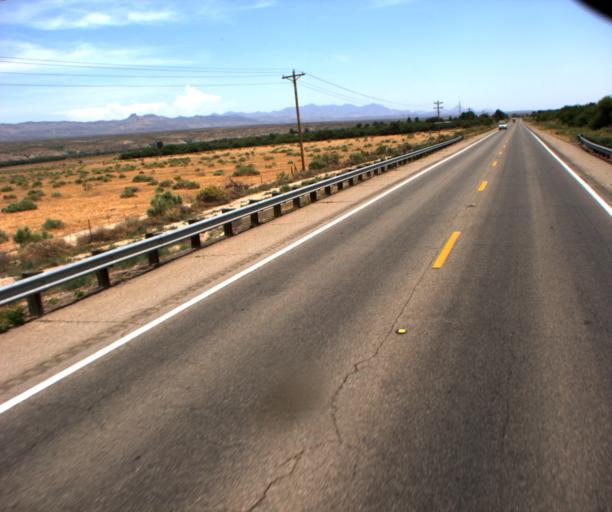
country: US
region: Arizona
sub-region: Graham County
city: Bylas
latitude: 33.0406
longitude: -109.9753
